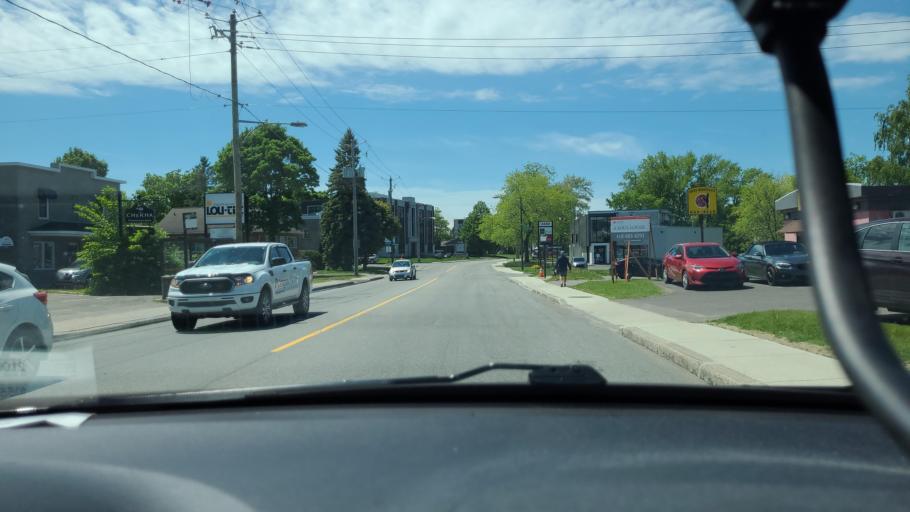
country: CA
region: Quebec
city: L'Ancienne-Lorette
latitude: 46.7694
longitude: -71.3209
